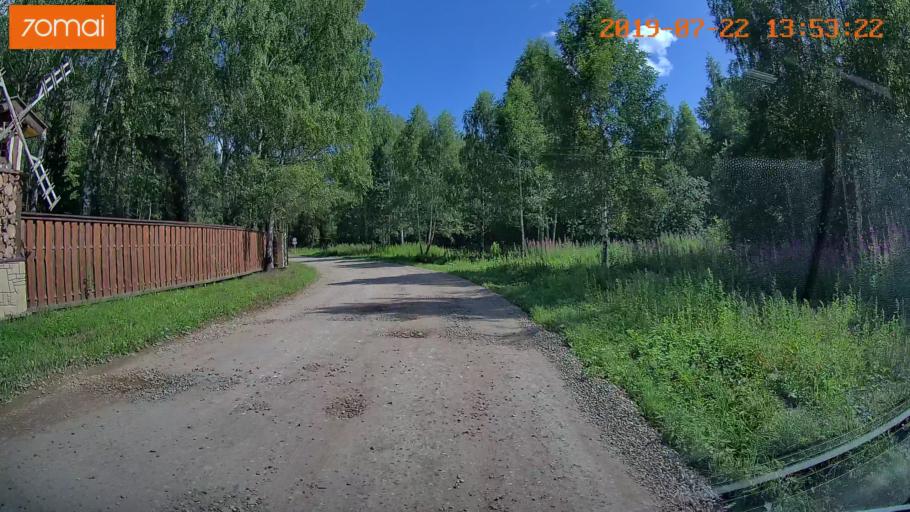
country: RU
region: Ivanovo
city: Novo-Talitsy
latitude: 57.0806
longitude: 40.8762
